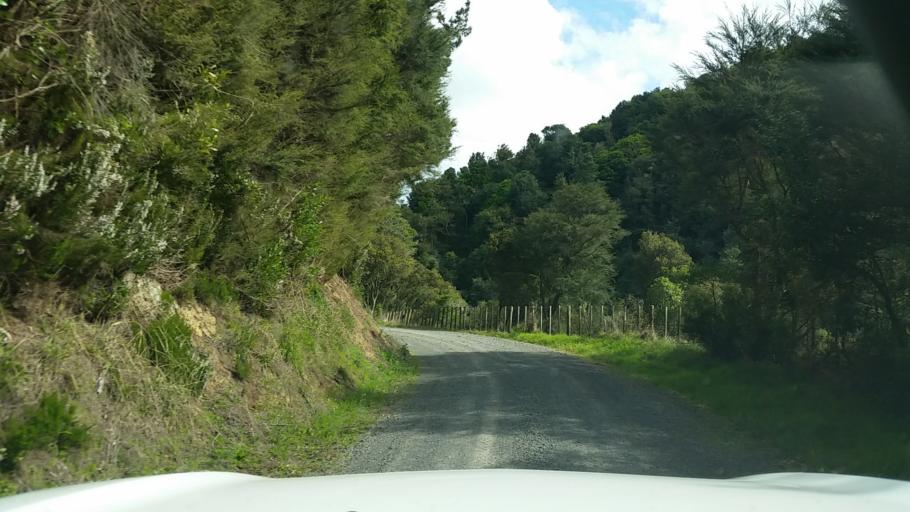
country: NZ
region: Waikato
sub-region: Hauraki District
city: Ngatea
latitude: -37.4778
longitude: 175.4550
